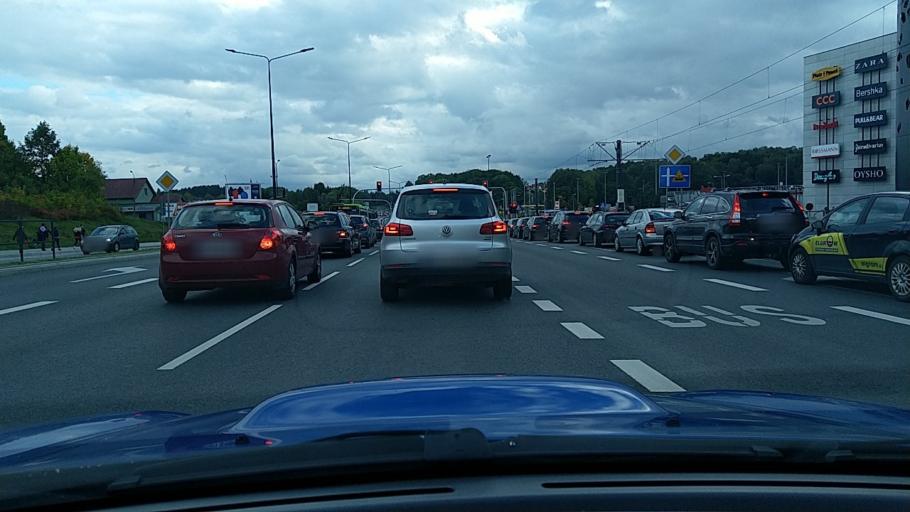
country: PL
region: Warmian-Masurian Voivodeship
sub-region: Powiat olsztynski
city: Olsztyn
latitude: 53.7538
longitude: 20.4861
